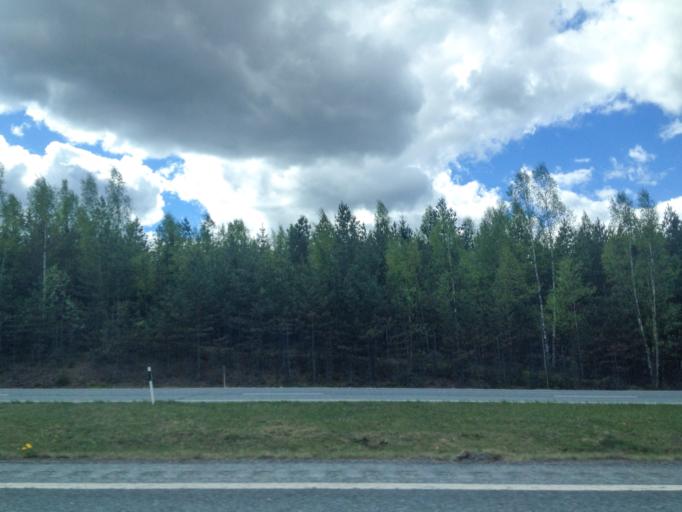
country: FI
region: Haeme
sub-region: Haemeenlinna
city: Kalvola
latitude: 61.1157
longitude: 24.1330
